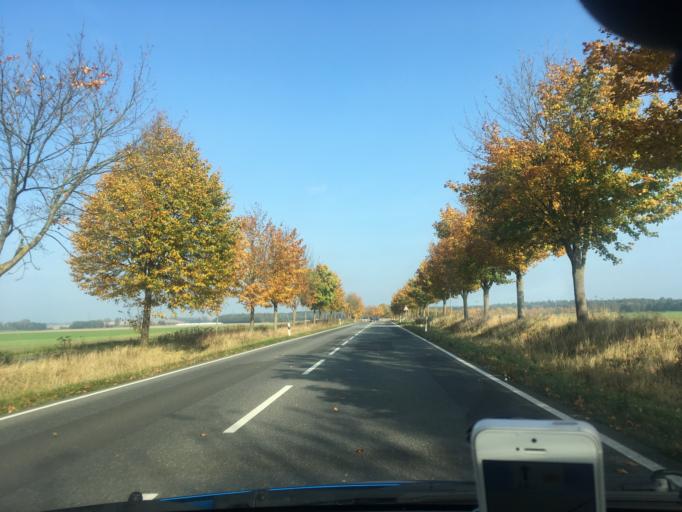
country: DE
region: Mecklenburg-Vorpommern
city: Stralendorf
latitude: 53.5368
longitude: 11.3049
